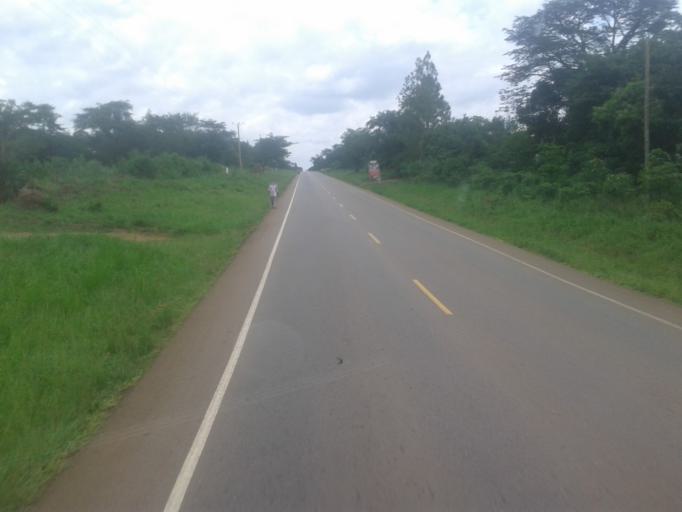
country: UG
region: Central Region
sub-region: Luwero District
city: Luwero
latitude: 1.0270
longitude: 32.4685
